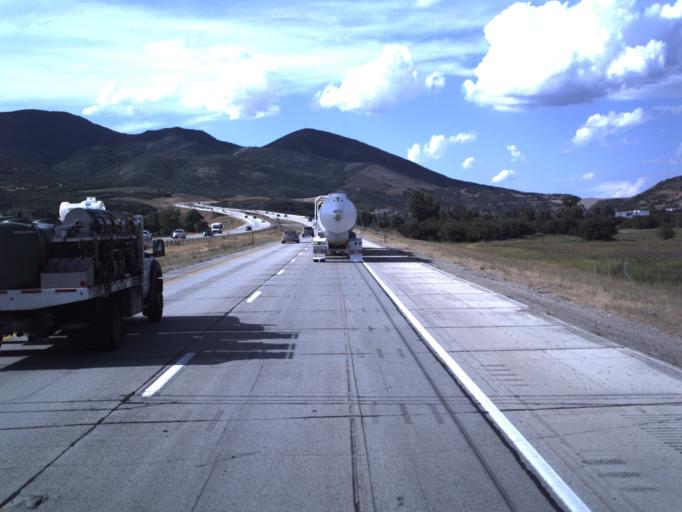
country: US
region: Utah
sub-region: Wasatch County
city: Heber
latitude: 40.5638
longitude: -111.4283
